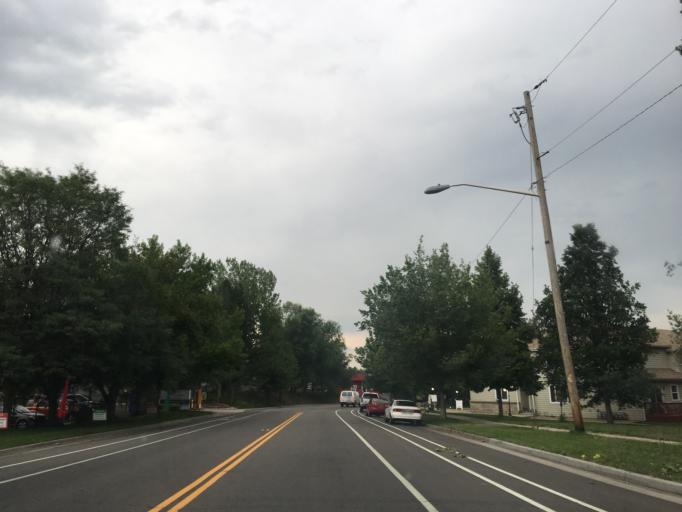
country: US
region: Colorado
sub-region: Arapahoe County
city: Sheridan
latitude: 39.6571
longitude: -105.0336
